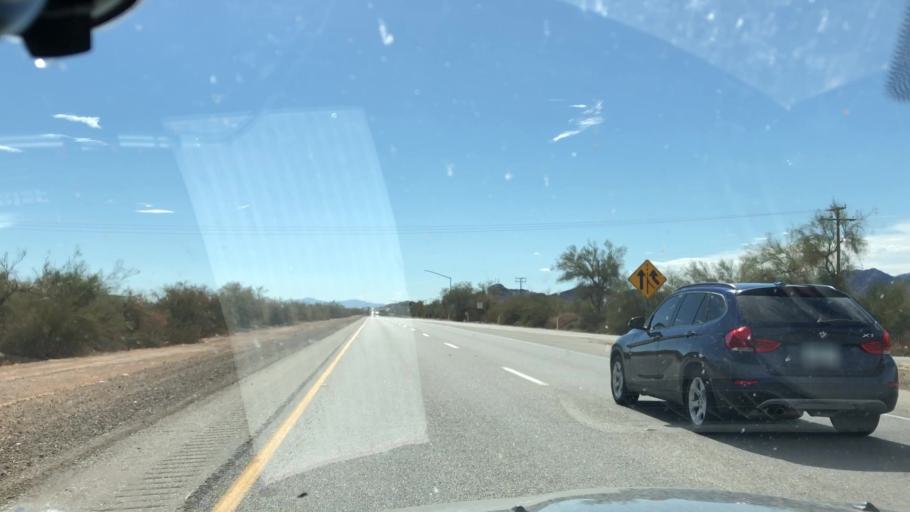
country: US
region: California
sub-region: Riverside County
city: Mesa Verde
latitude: 33.6096
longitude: -114.7298
